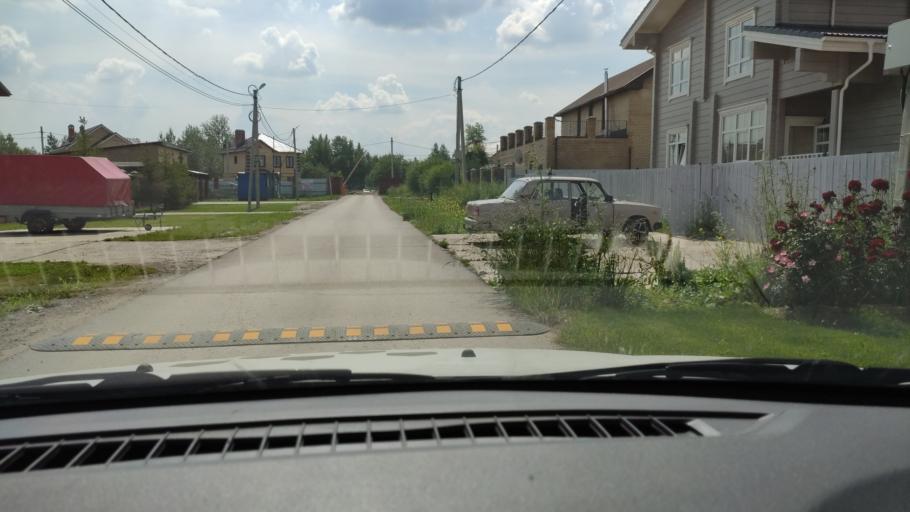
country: RU
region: Perm
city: Perm
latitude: 58.0376
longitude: 56.3738
